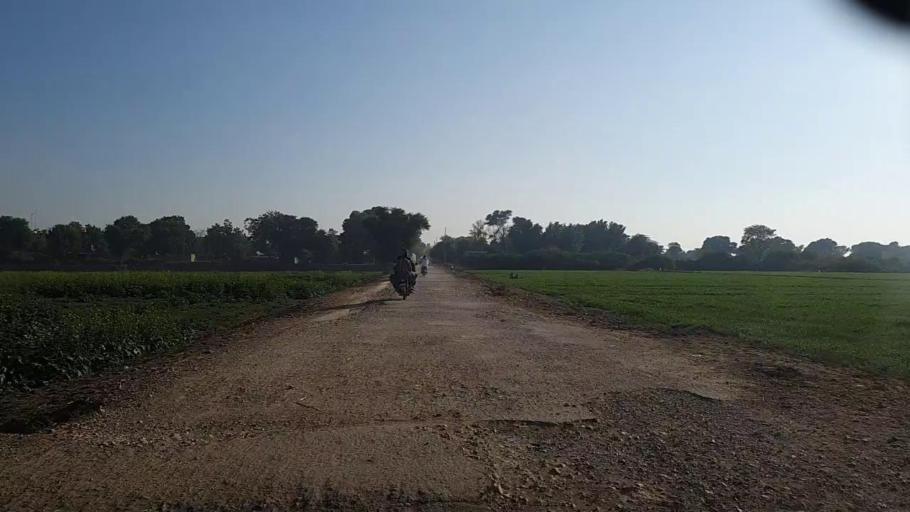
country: PK
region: Sindh
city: Darya Khan Marri
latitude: 26.6986
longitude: 68.3625
